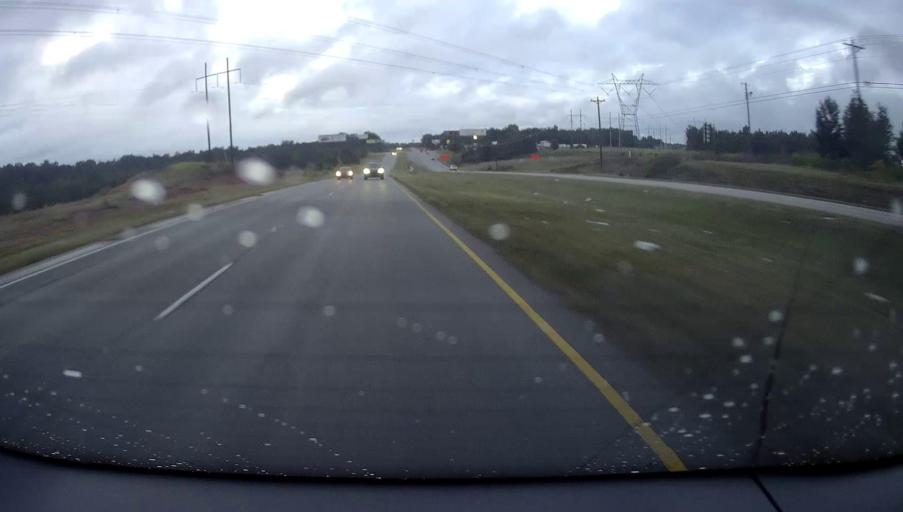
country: US
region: Georgia
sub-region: Houston County
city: Centerville
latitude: 32.6142
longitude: -83.7193
